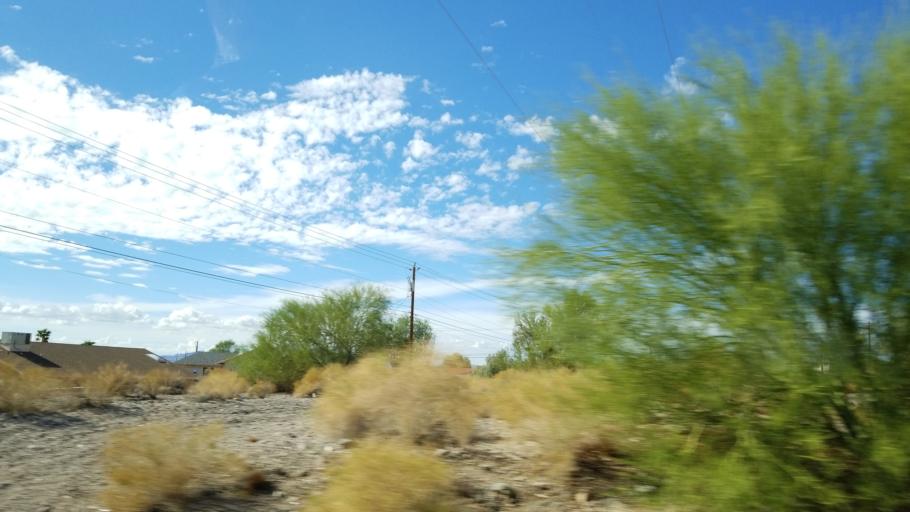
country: US
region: Arizona
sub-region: Mohave County
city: Lake Havasu City
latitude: 34.4962
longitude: -114.2886
